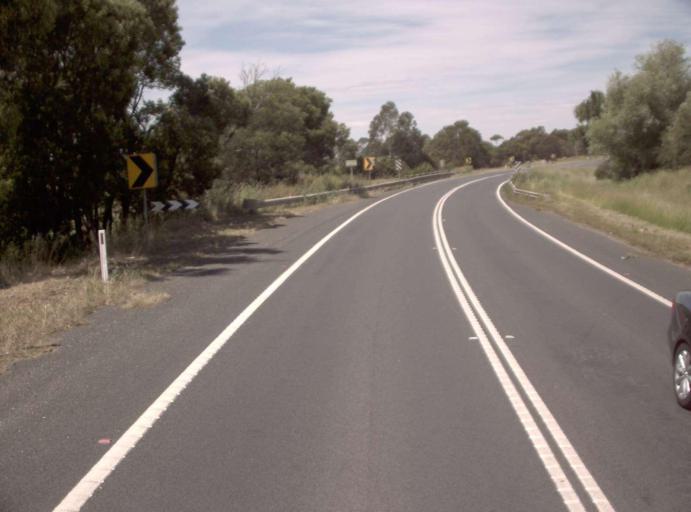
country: AU
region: Victoria
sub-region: Latrobe
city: Traralgon
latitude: -38.1579
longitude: 146.7100
